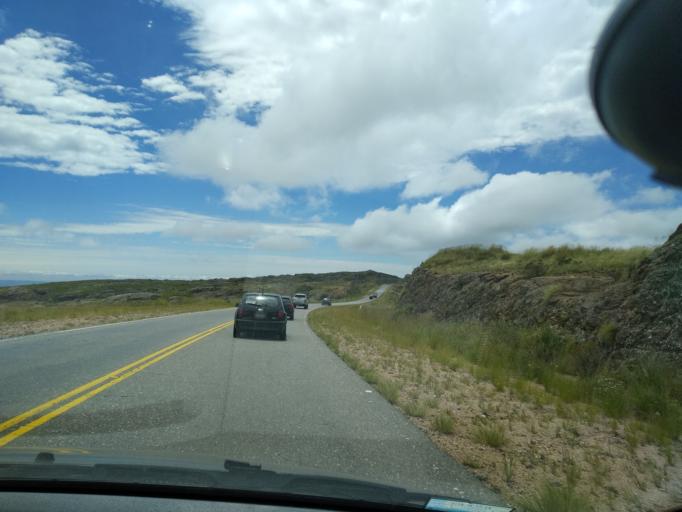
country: AR
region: Cordoba
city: Cuesta Blanca
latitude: -31.6091
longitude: -64.7374
